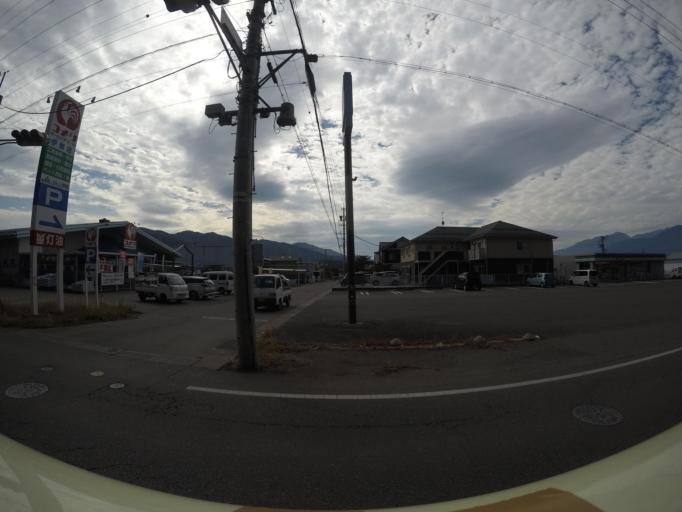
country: JP
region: Nagano
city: Ina
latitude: 35.8374
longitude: 137.9997
